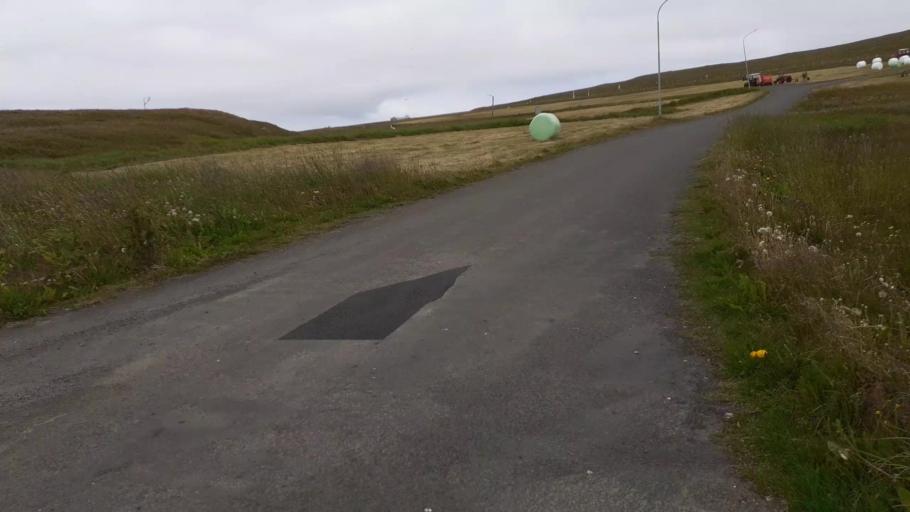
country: IS
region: Northeast
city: Dalvik
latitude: 66.5404
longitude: -18.0171
